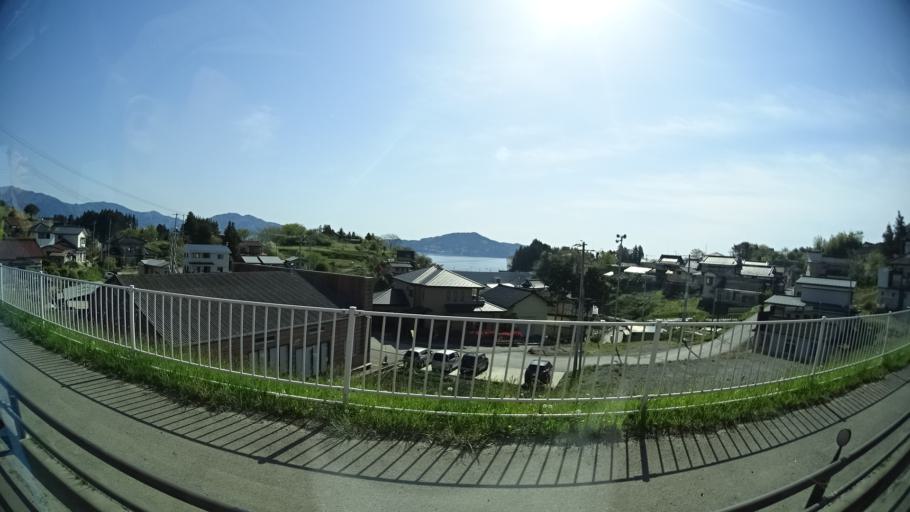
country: JP
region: Iwate
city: Ofunato
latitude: 38.9815
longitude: 141.6213
